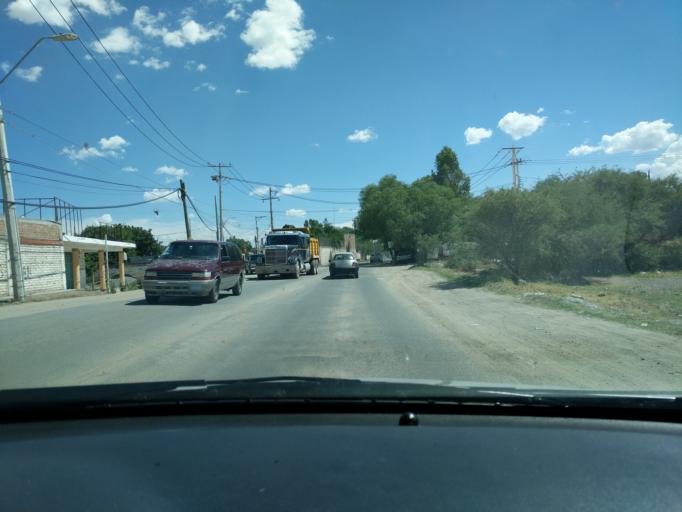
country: MX
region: Guanajuato
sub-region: Leon
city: Ladrilleras del Refugio
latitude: 21.0731
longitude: -101.5483
